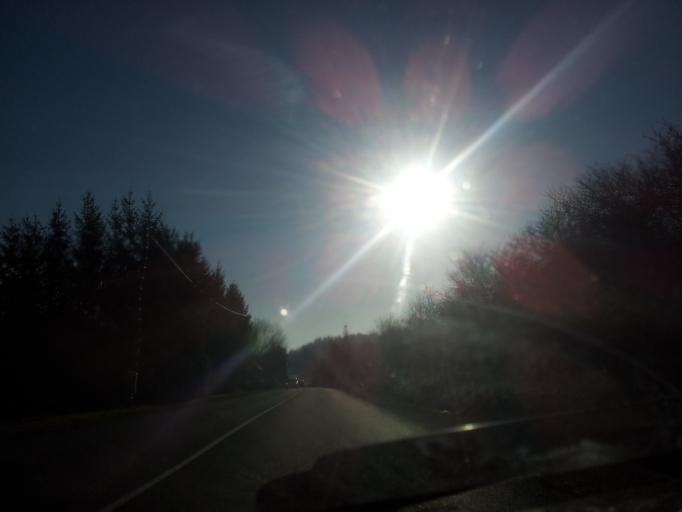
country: FR
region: Auvergne
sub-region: Departement de l'Allier
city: Saint-Pourcain-sur-Sioule
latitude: 46.3186
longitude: 3.2415
